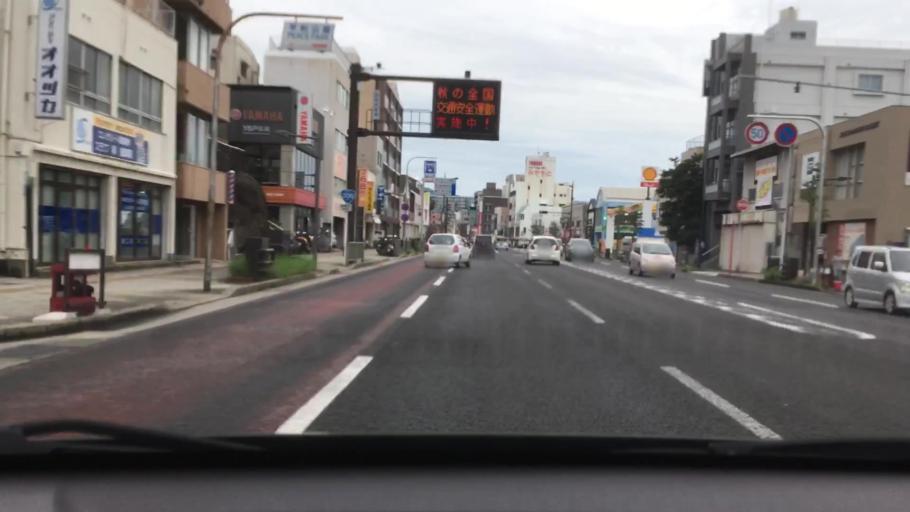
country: JP
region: Nagasaki
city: Nagasaki-shi
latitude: 32.7770
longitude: 129.8620
